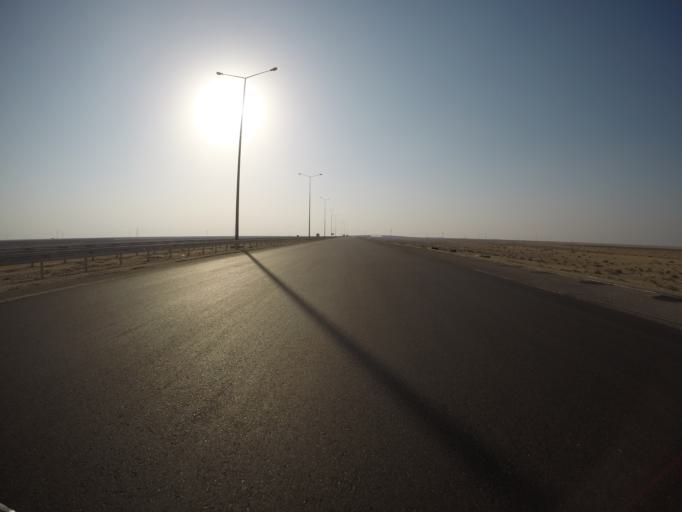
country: IQ
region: Dhi Qar
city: Suq ash Shuyukh
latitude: 30.6628
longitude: 46.5194
